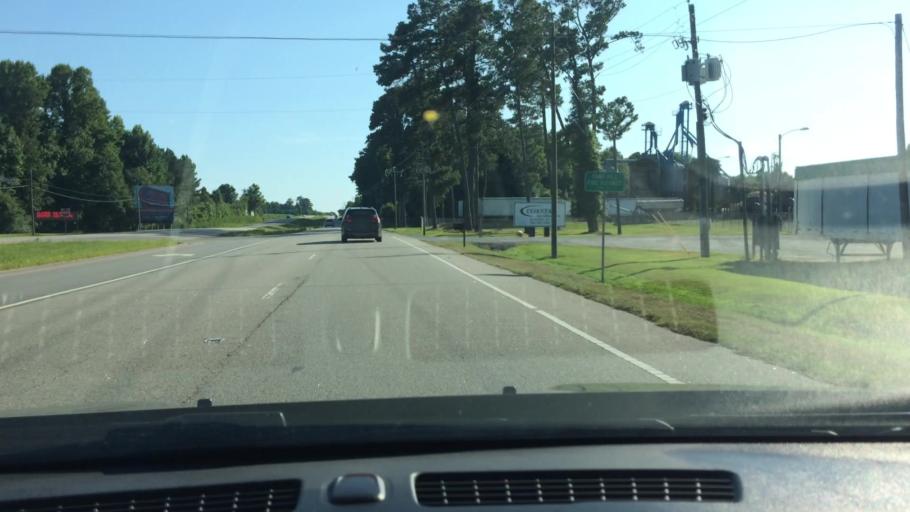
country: US
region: North Carolina
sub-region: Lenoir County
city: Kinston
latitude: 35.3067
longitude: -77.5271
